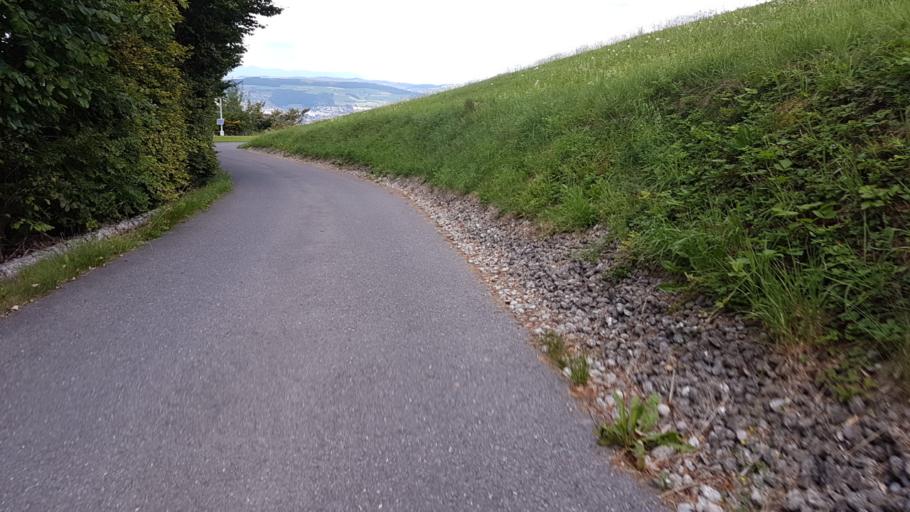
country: CH
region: Lucerne
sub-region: Entlebuch District
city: Oberdiessbach
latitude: 46.8234
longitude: 7.6371
